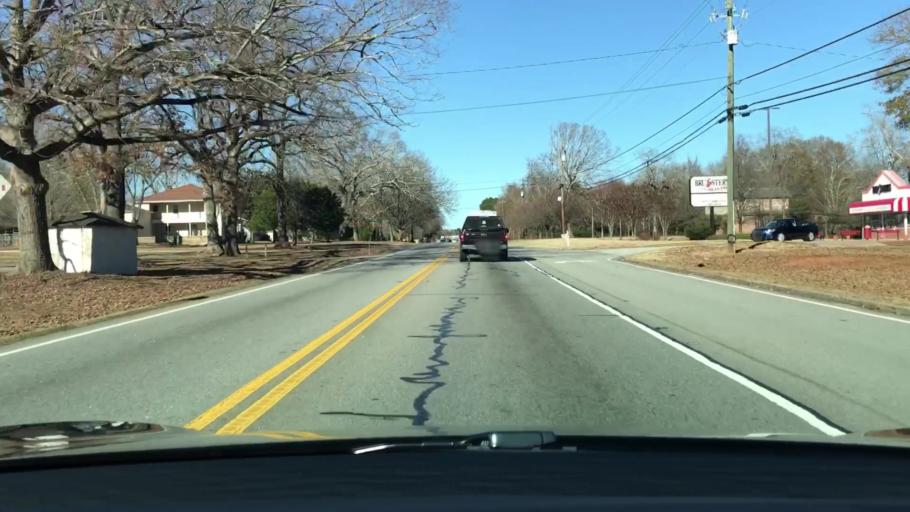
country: US
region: Georgia
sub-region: Walton County
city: Monroe
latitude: 33.8234
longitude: -83.7323
